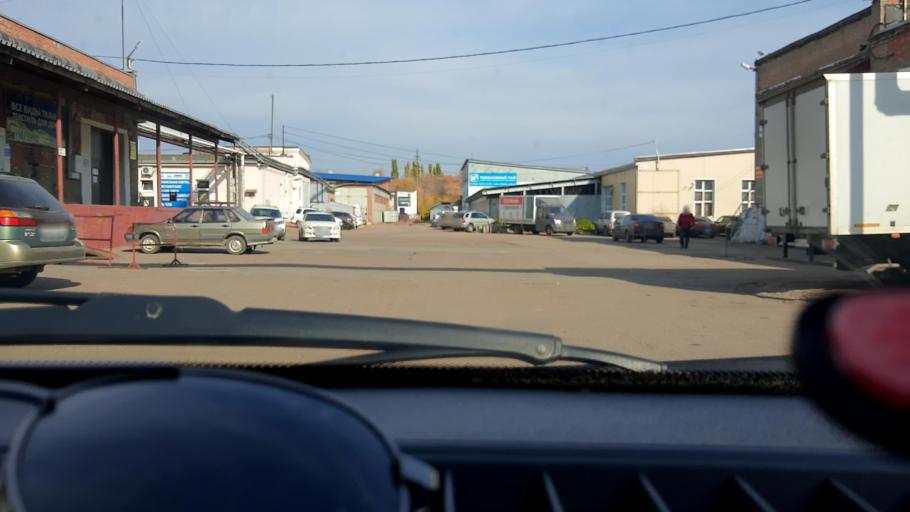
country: RU
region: Bashkortostan
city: Ufa
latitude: 54.7954
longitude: 56.0615
